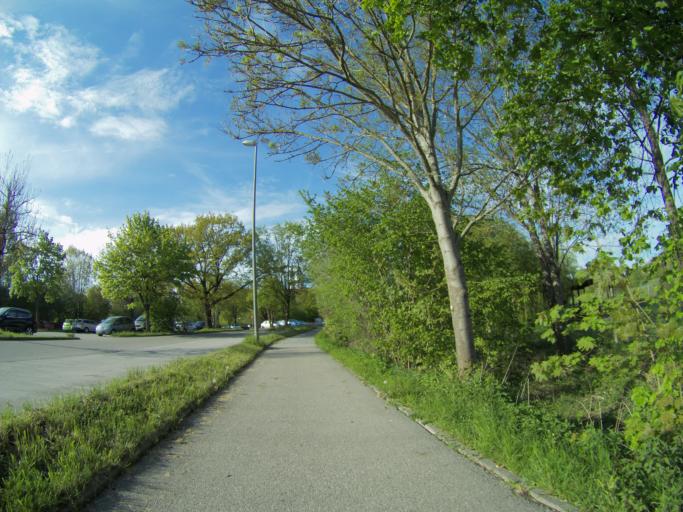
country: DE
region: Bavaria
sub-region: Upper Bavaria
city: Freising
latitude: 48.3947
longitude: 11.7458
